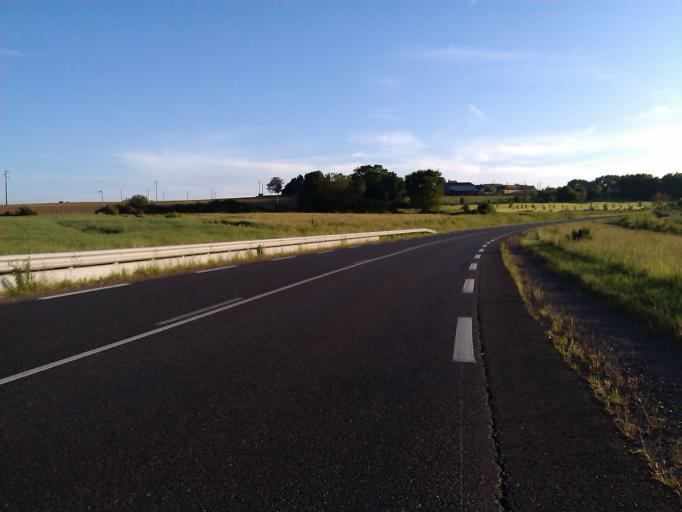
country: FR
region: Poitou-Charentes
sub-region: Departement de la Vienne
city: Saint-Savin
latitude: 46.5940
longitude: 0.9680
